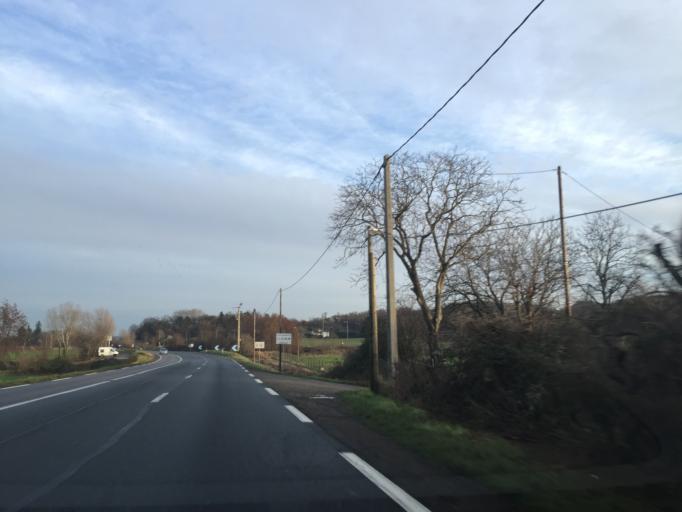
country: FR
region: Rhone-Alpes
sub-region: Departement de l'Isere
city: Vaulx-Milieu
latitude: 45.6124
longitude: 5.2017
